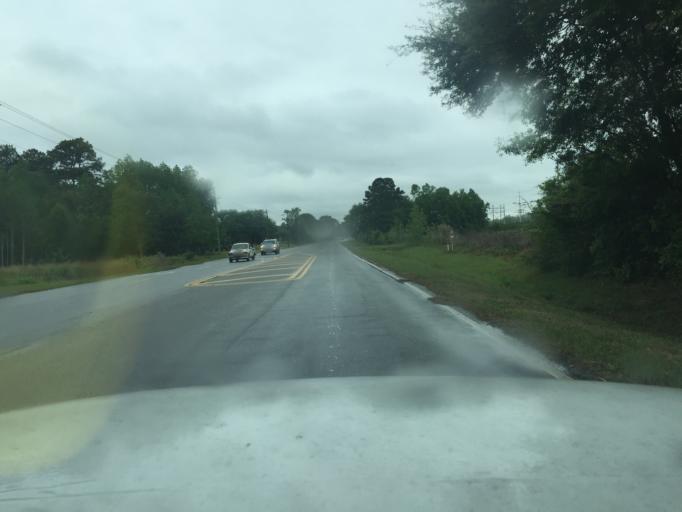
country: US
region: Georgia
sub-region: Chatham County
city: Georgetown
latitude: 32.0038
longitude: -81.2473
